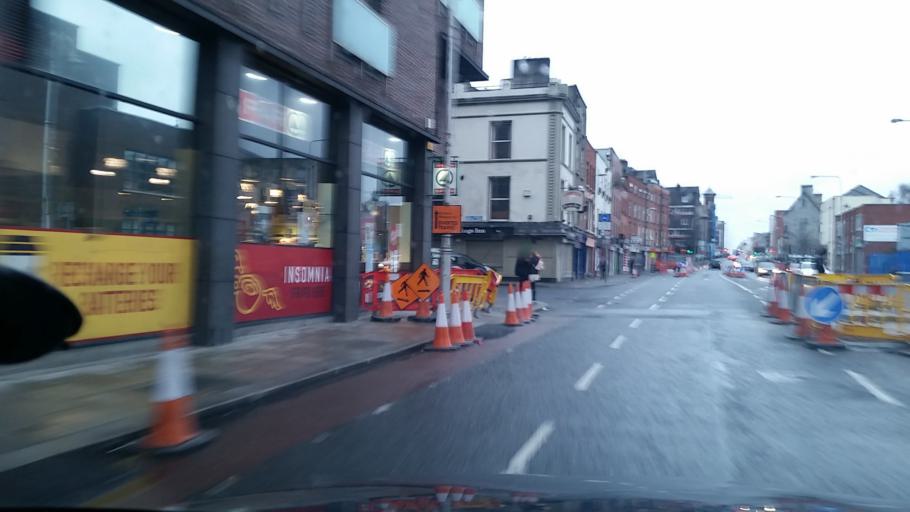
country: IE
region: Leinster
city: Drumcondra
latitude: 53.3519
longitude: -6.2694
